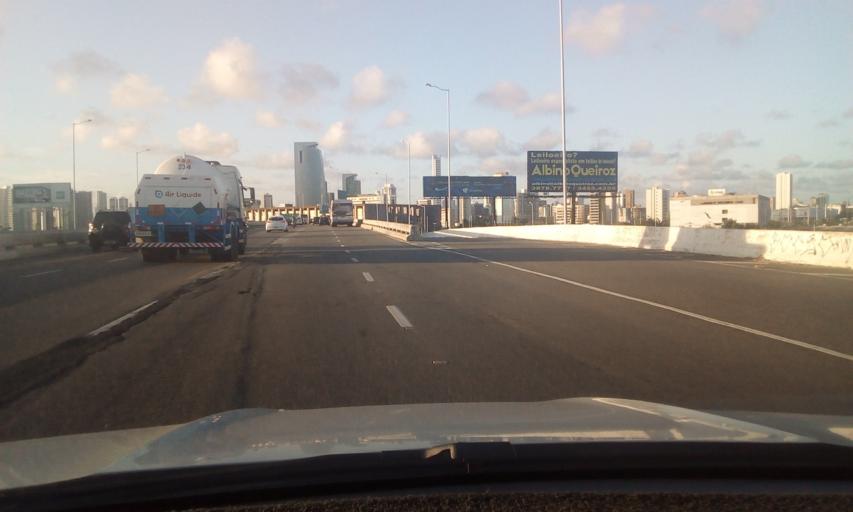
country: BR
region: Pernambuco
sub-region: Recife
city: Recife
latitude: -8.0750
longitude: -34.8932
